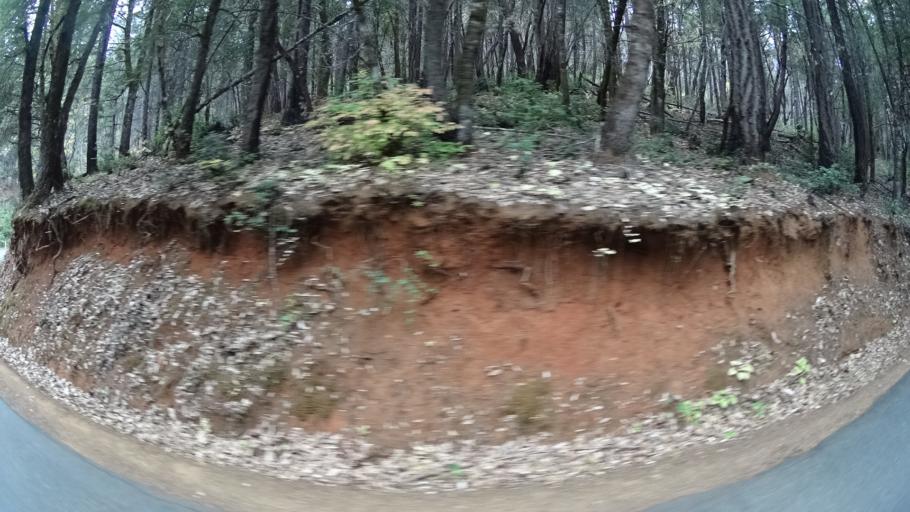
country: US
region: California
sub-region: Siskiyou County
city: Happy Camp
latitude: 41.8022
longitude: -123.3541
